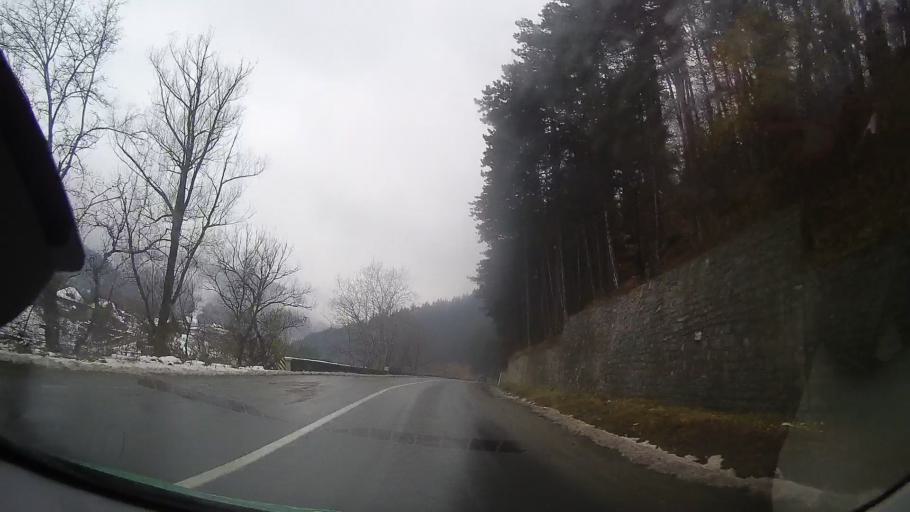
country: RO
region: Neamt
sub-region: Comuna Tarcau
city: Tarcau
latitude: 46.8921
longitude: 26.1409
